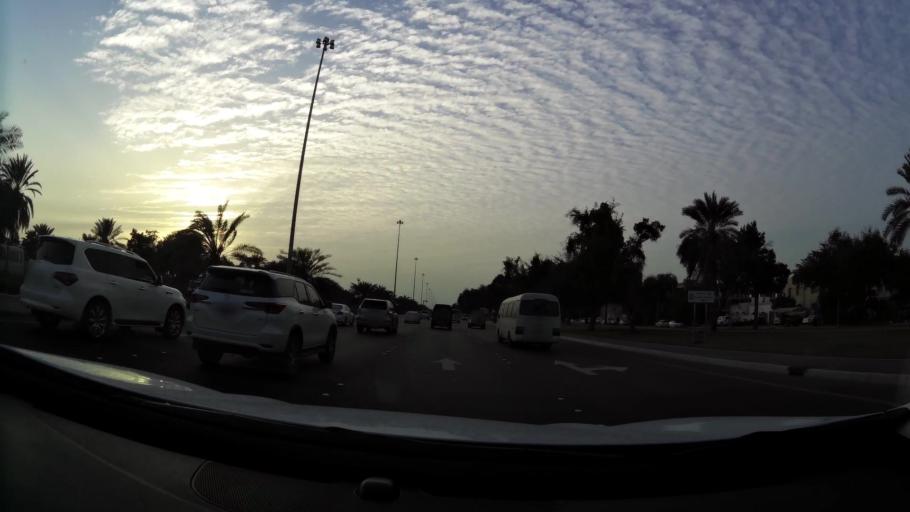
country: AE
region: Abu Dhabi
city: Abu Dhabi
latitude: 24.4267
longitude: 54.4028
